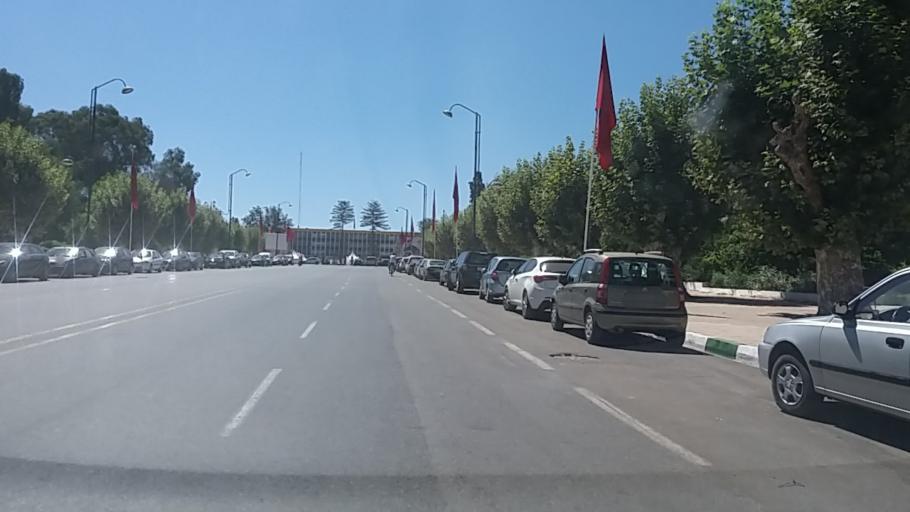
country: MA
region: Gharb-Chrarda-Beni Hssen
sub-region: Kenitra Province
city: Kenitra
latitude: 34.2580
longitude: -6.5801
